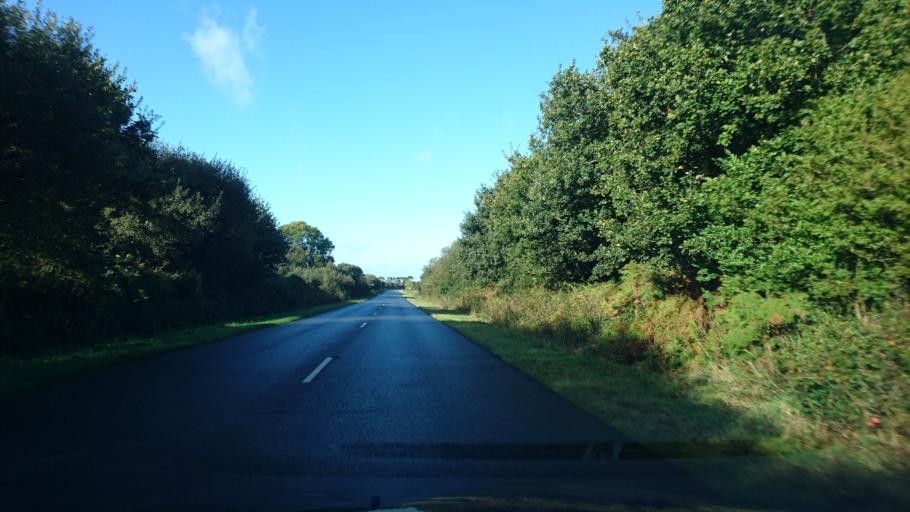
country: FR
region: Brittany
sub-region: Departement du Finistere
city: Plouarzel
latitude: 48.4385
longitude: -4.7230
